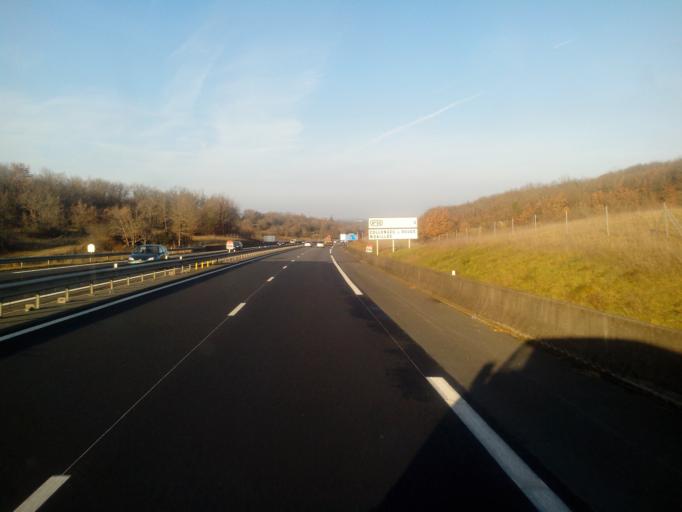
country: FR
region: Limousin
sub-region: Departement de la Correze
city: Brive-la-Gaillarde
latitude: 45.0682
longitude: 1.5076
